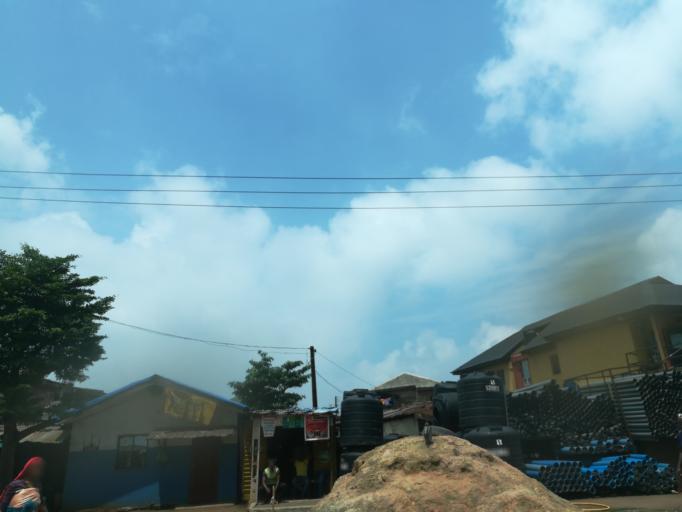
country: NG
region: Lagos
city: Ikorodu
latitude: 6.6645
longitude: 3.5181
